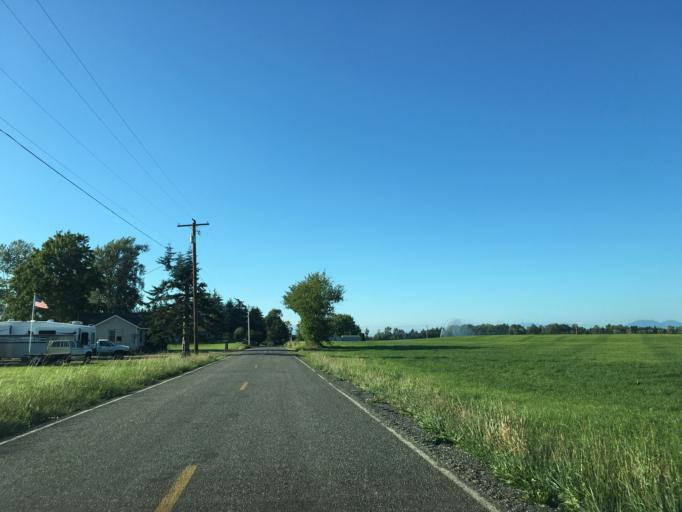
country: US
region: Washington
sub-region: Whatcom County
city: Everson
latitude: 48.9390
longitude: -122.3916
